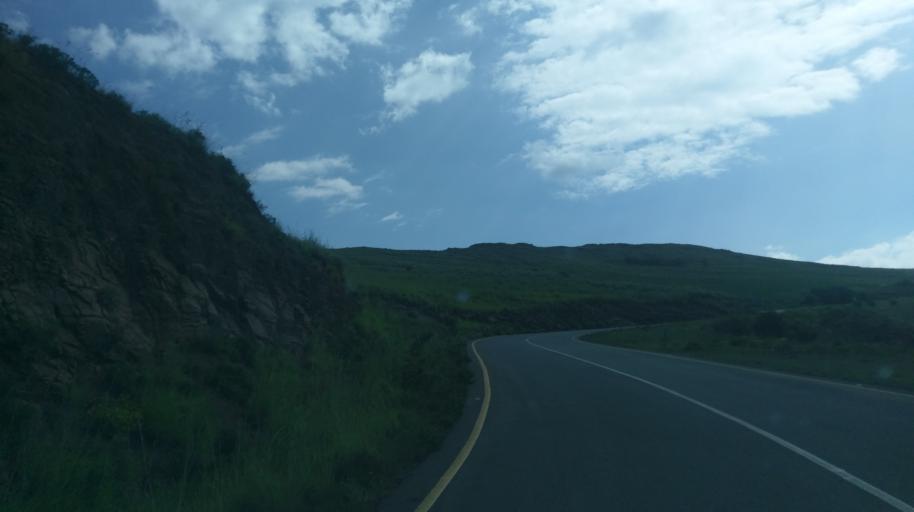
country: LS
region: Thaba-Tseka
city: Thaba-Tseka
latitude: -29.1569
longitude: 28.4842
